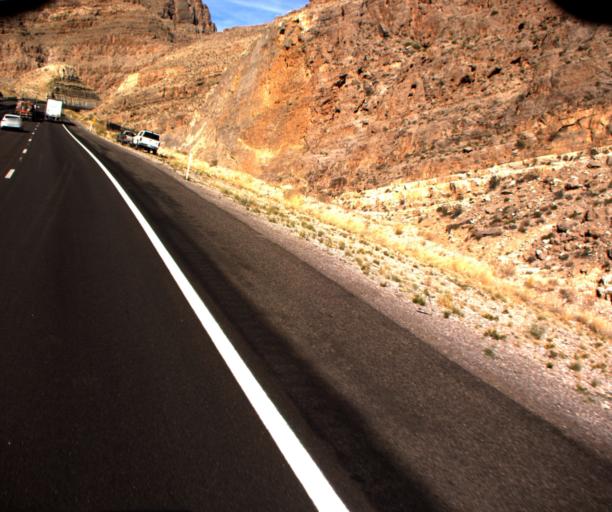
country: US
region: Arizona
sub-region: Mohave County
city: Beaver Dam
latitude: 36.9218
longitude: -113.8320
